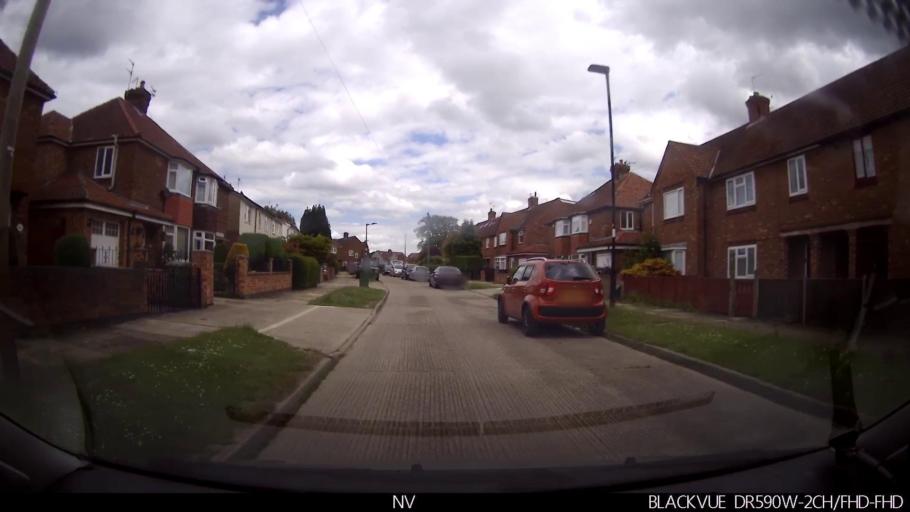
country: GB
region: England
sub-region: City of York
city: Bishopthorpe
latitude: 53.9385
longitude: -1.1174
